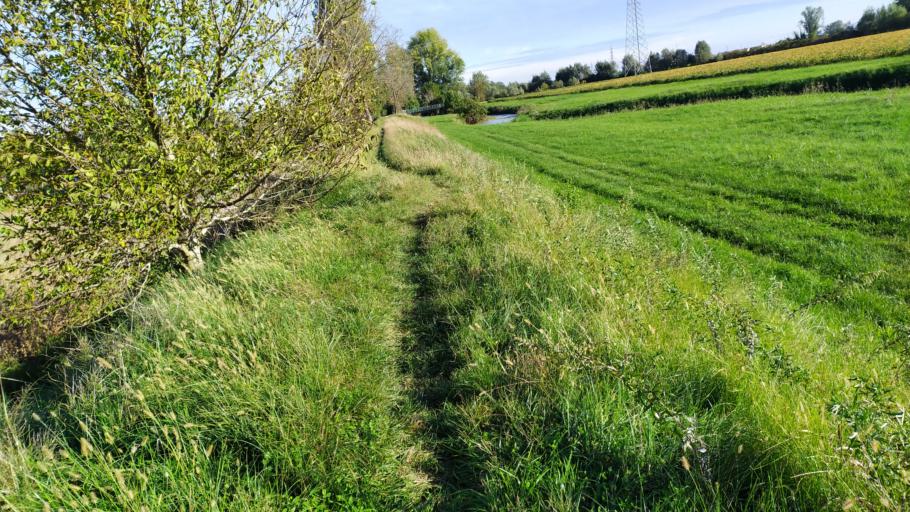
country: IT
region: Veneto
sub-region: Provincia di Vicenza
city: Caldogno-Rettorgole-Cresole
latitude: 45.6231
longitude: 11.5249
